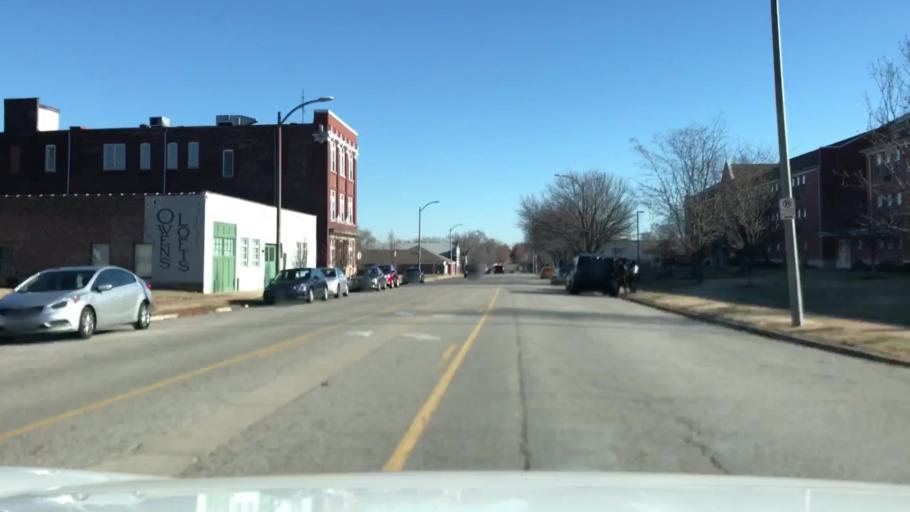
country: US
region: Missouri
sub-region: City of Saint Louis
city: St. Louis
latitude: 38.6200
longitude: -90.2338
